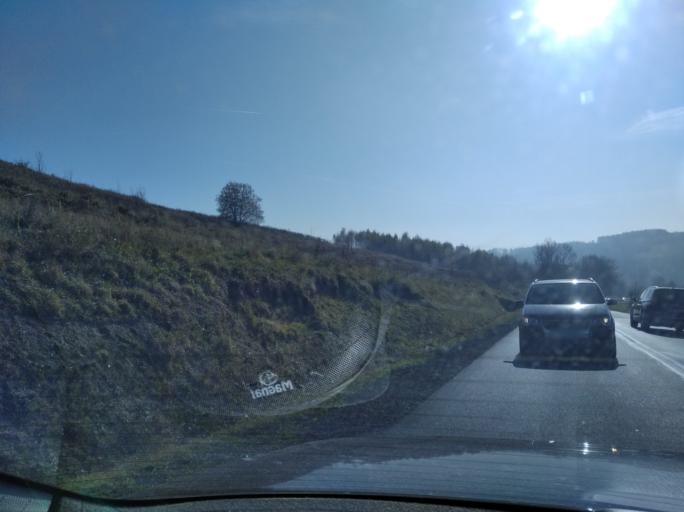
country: PL
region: Subcarpathian Voivodeship
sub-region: Powiat ropczycko-sedziszowski
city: Wielopole Skrzynskie
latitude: 49.9123
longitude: 21.6184
